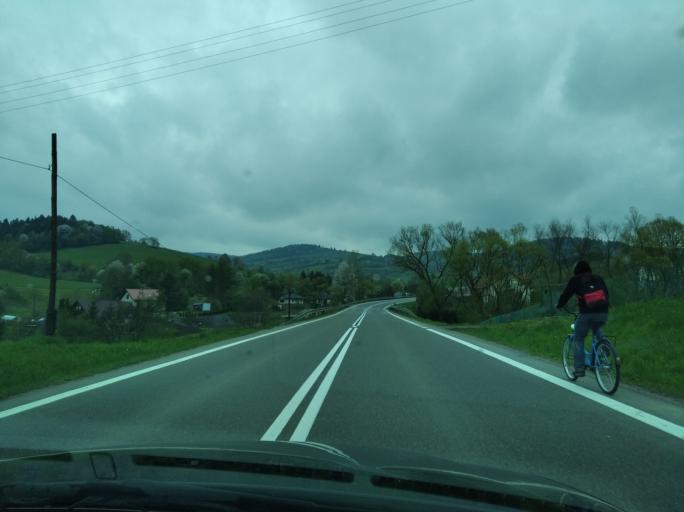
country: PL
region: Subcarpathian Voivodeship
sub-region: Powiat sanocki
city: Zagorz
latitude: 49.5426
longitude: 22.3022
